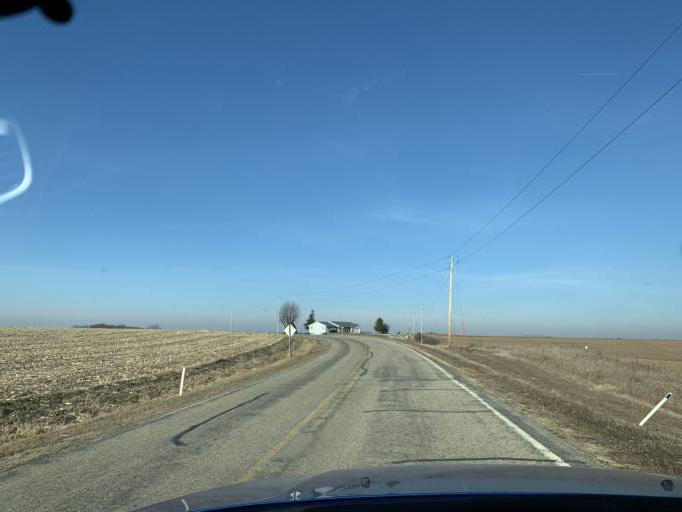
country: US
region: Wisconsin
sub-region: Iowa County
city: Barneveld
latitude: 42.8173
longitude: -89.9166
